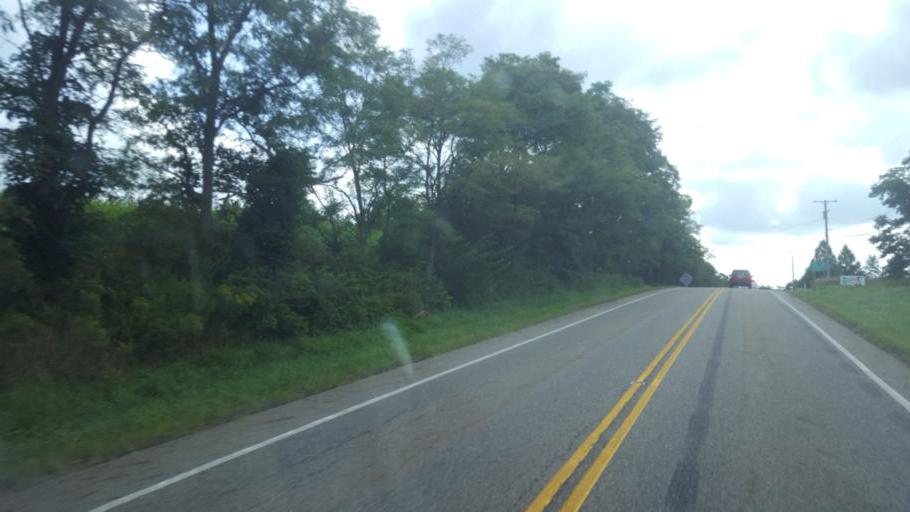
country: US
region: Ohio
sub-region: Stark County
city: Louisville
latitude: 40.8006
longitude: -81.1853
